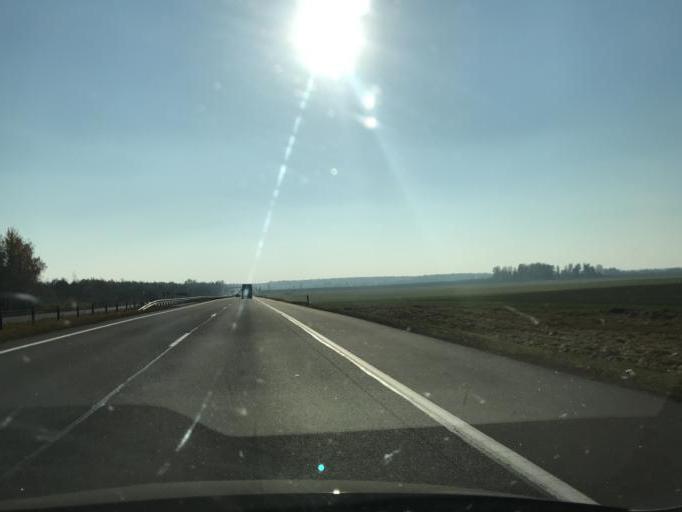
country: BY
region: Minsk
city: Enyerhyetykaw
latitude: 53.6168
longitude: 27.0508
